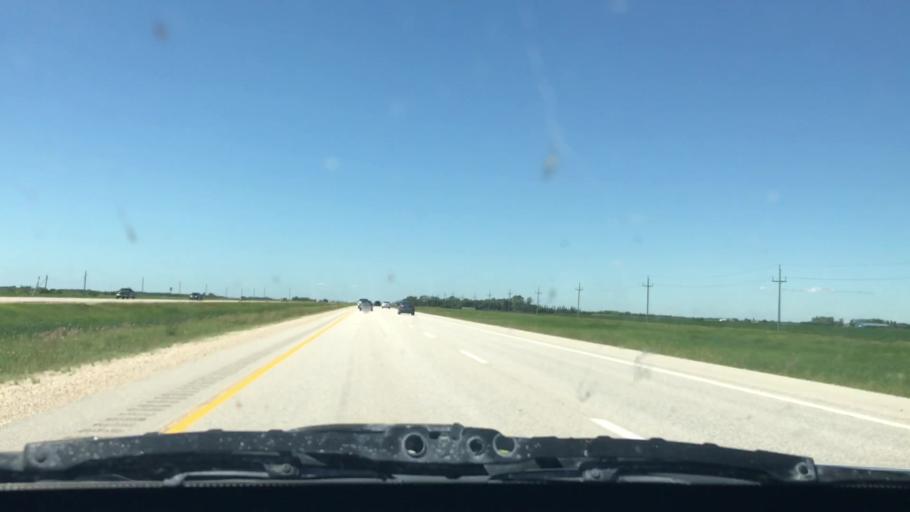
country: CA
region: Manitoba
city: Steinbach
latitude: 49.7359
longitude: -96.7329
